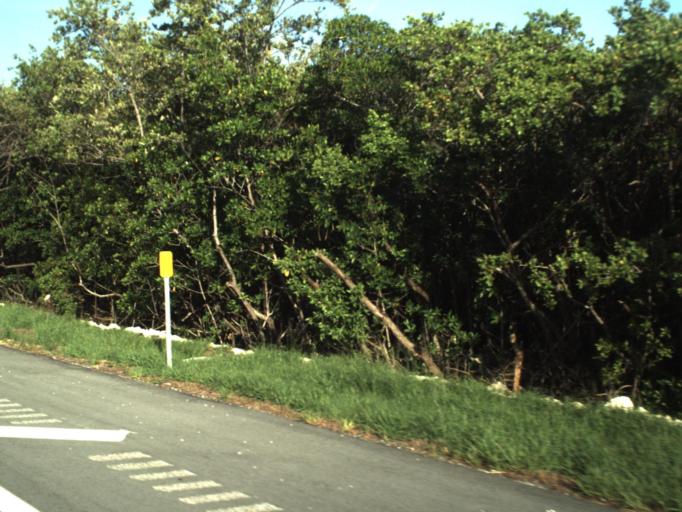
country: US
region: Florida
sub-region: Monroe County
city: Marathon
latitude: 24.7510
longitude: -80.9712
